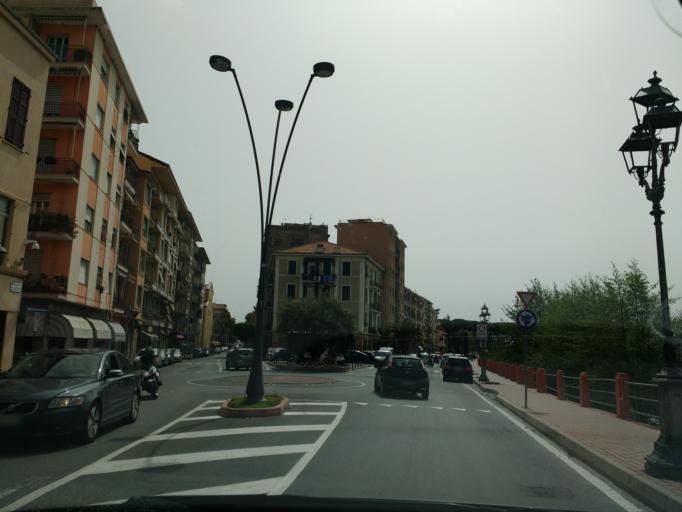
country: IT
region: Liguria
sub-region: Provincia di Imperia
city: Ventimiglia
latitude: 43.7922
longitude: 7.6056
